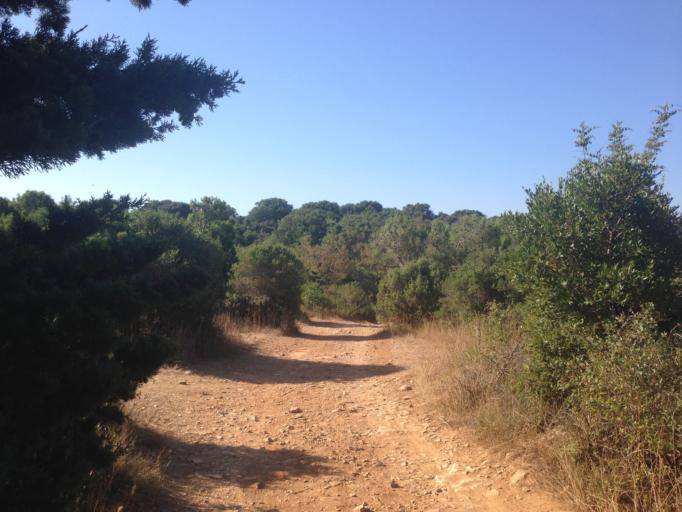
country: HR
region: Istarska
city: Medulin
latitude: 44.7870
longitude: 13.9074
